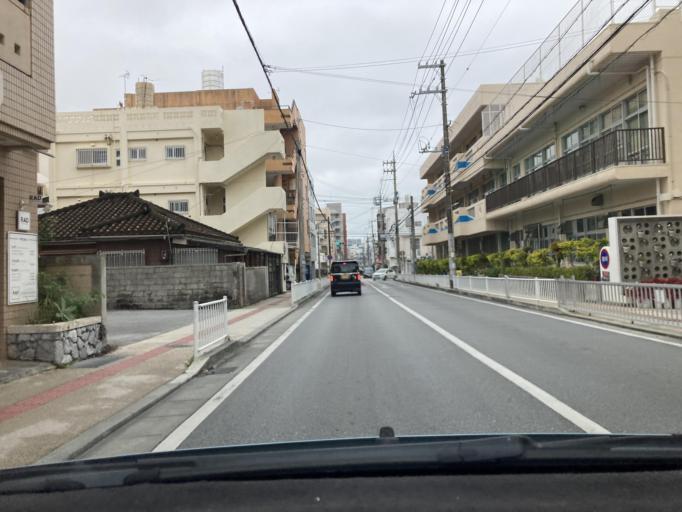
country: JP
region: Okinawa
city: Naha-shi
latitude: 26.2243
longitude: 127.6889
